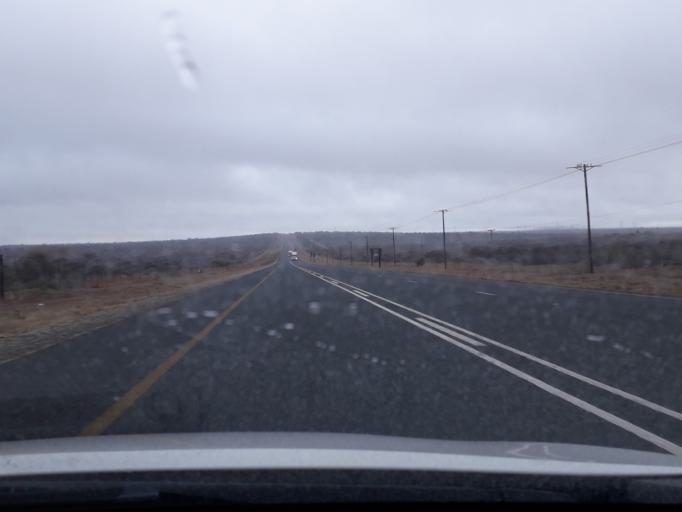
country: ZA
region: Limpopo
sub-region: Vhembe District Municipality
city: Louis Trichardt
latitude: -23.3990
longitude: 29.7599
